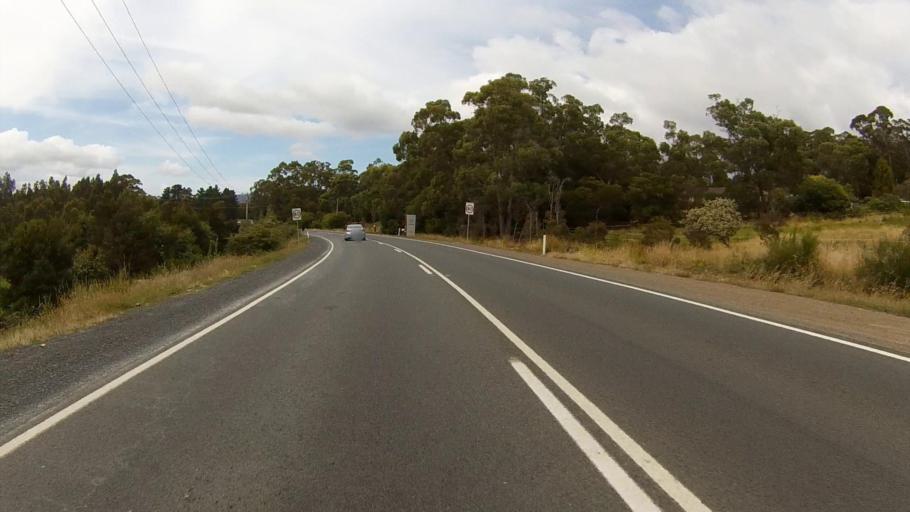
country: AU
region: Tasmania
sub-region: Kingborough
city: Margate
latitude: -43.0380
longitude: 147.2659
